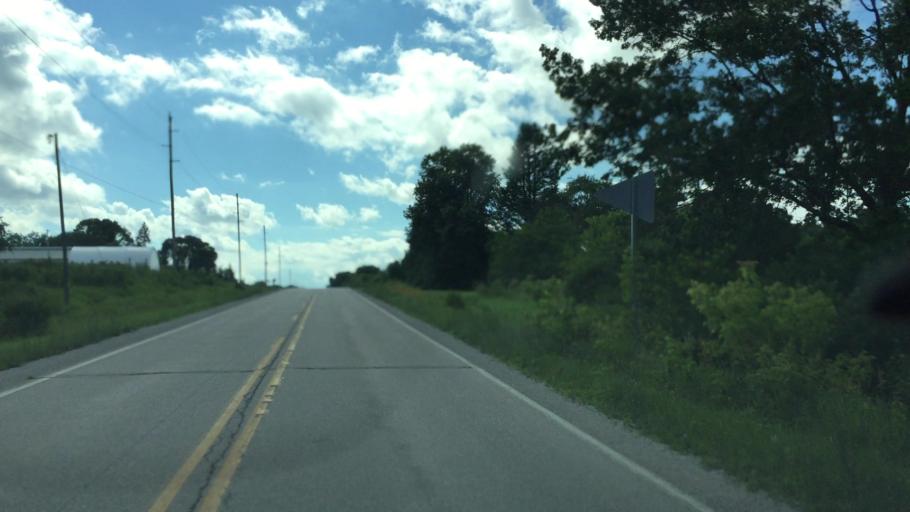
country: US
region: Iowa
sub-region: Linn County
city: Ely
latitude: 41.8474
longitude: -91.6022
